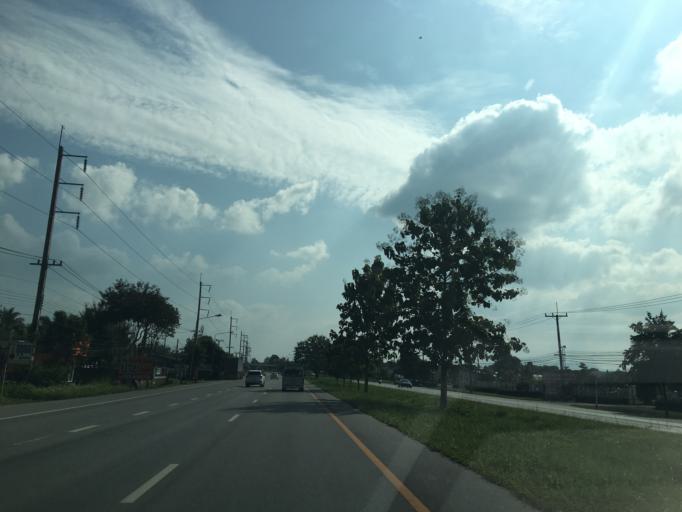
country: TH
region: Chiang Rai
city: Mae Lao
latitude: 19.7248
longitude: 99.7163
